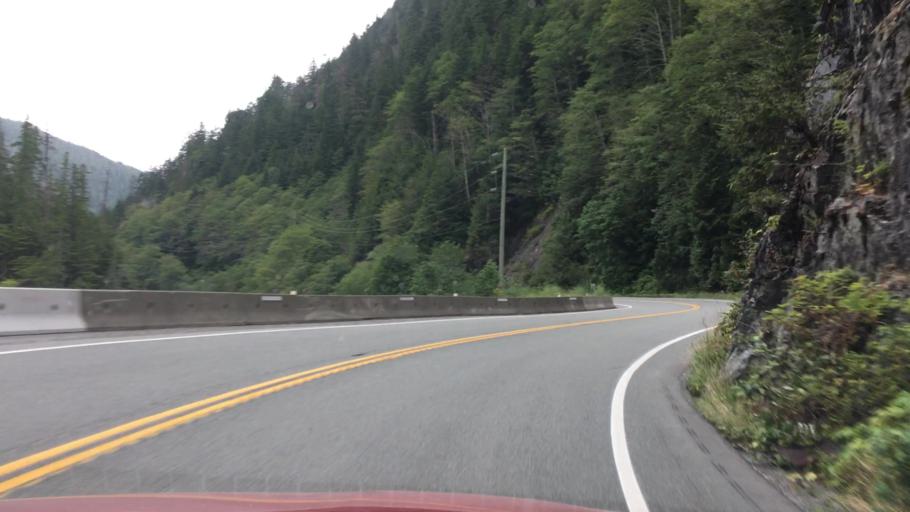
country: CA
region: British Columbia
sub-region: Regional District of Alberni-Clayoquot
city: Ucluelet
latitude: 49.1508
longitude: -125.4224
